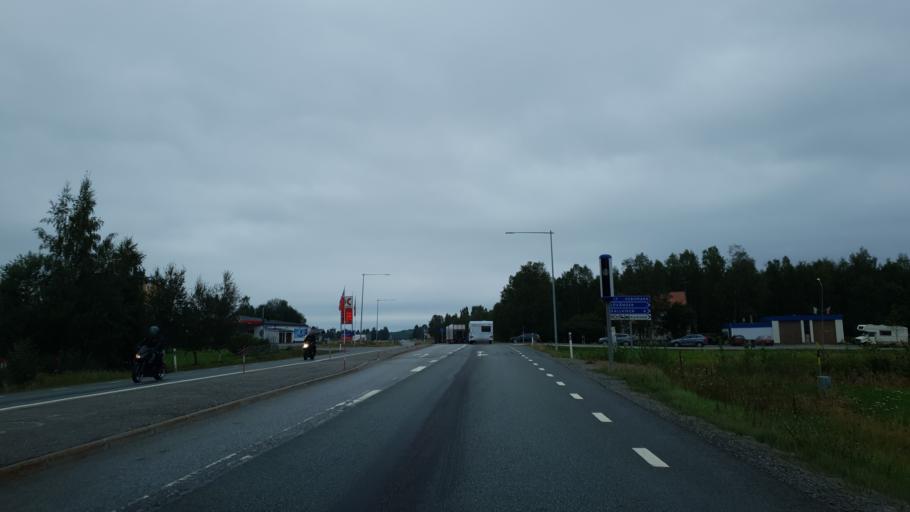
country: SE
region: Vaesterbotten
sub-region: Skelleftea Kommun
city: Burea
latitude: 64.3714
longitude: 21.3025
